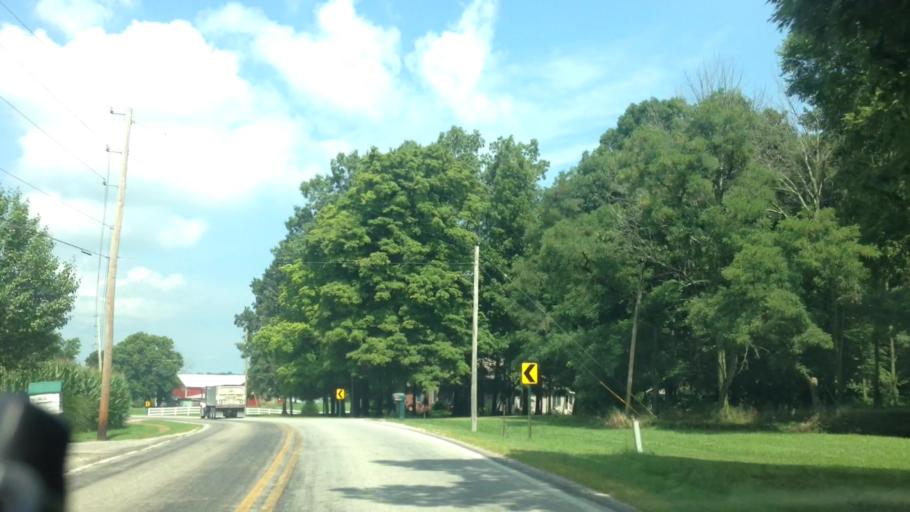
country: US
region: Ohio
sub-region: Wayne County
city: Dalton
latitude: 40.8623
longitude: -81.6675
